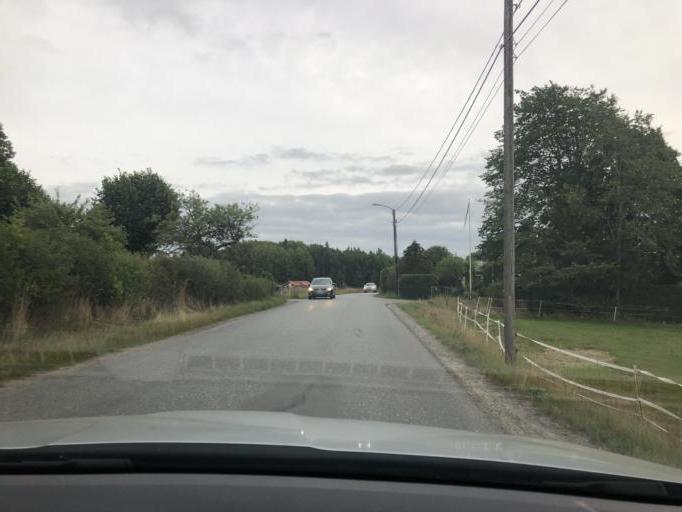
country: SE
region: Stockholm
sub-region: Haninge Kommun
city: Jordbro
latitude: 59.0961
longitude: 18.0366
